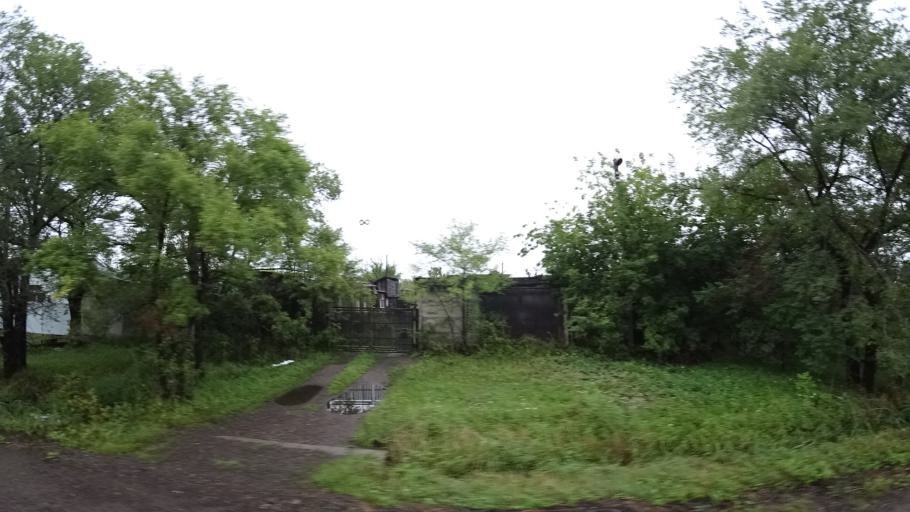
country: RU
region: Primorskiy
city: Monastyrishche
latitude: 44.2003
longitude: 132.4583
